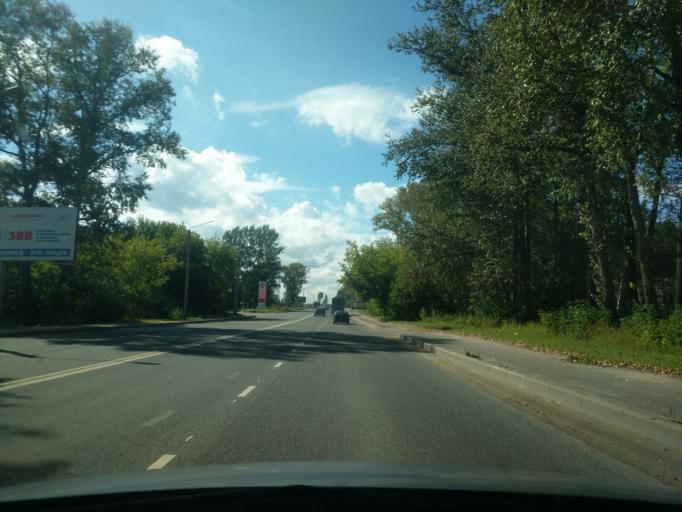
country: RU
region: Kostroma
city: Oktyabr'skiy
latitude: 57.7804
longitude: 40.9803
